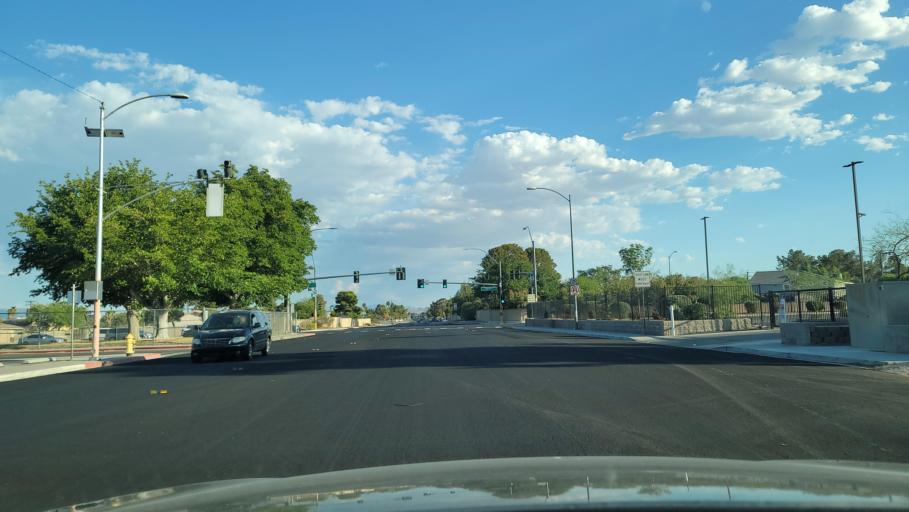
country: US
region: Nevada
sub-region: Clark County
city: Spring Valley
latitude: 36.1527
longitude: -115.2168
